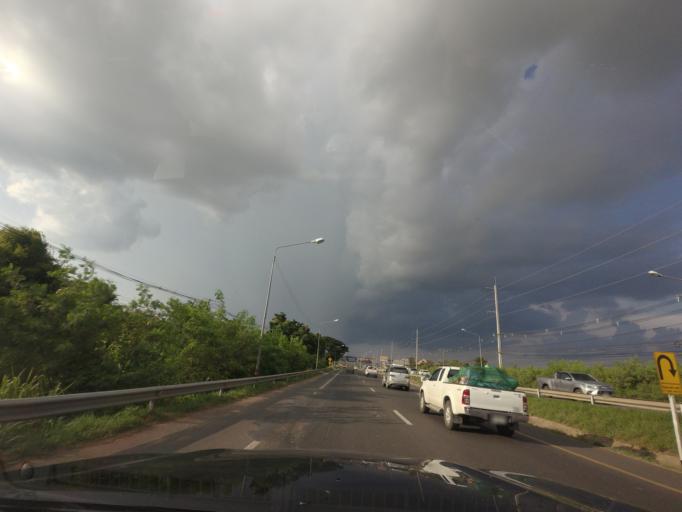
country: TH
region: Khon Kaen
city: Khon Kaen
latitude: 16.3592
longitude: 102.8045
